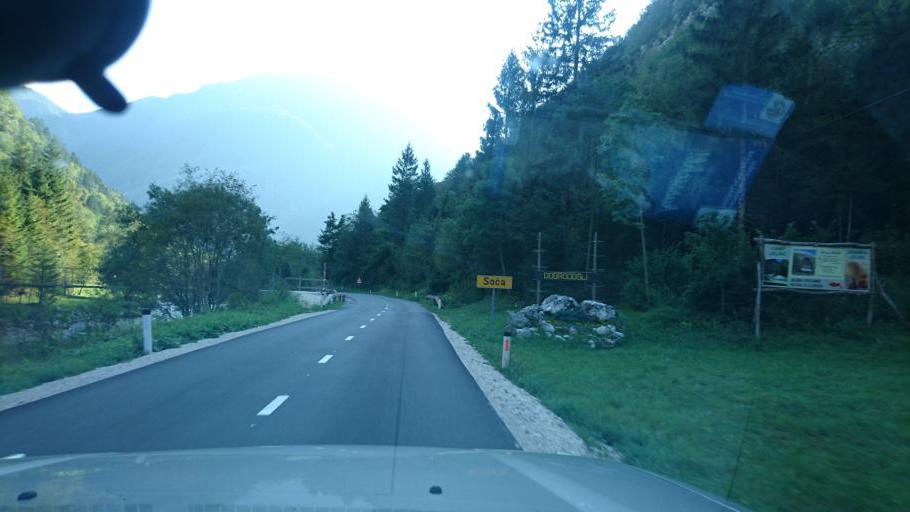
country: SI
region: Bovec
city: Bovec
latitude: 46.3485
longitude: 13.6902
